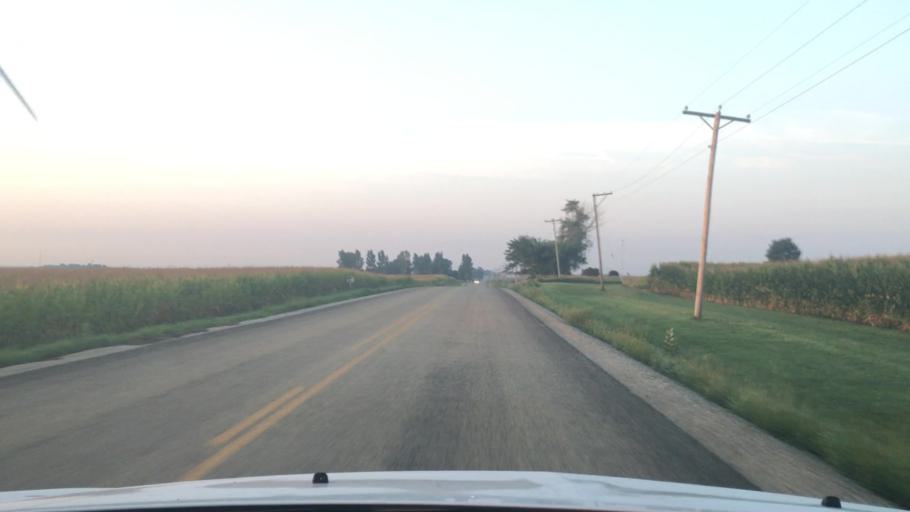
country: US
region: Illinois
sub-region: DeKalb County
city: Waterman
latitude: 41.8264
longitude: -88.7733
